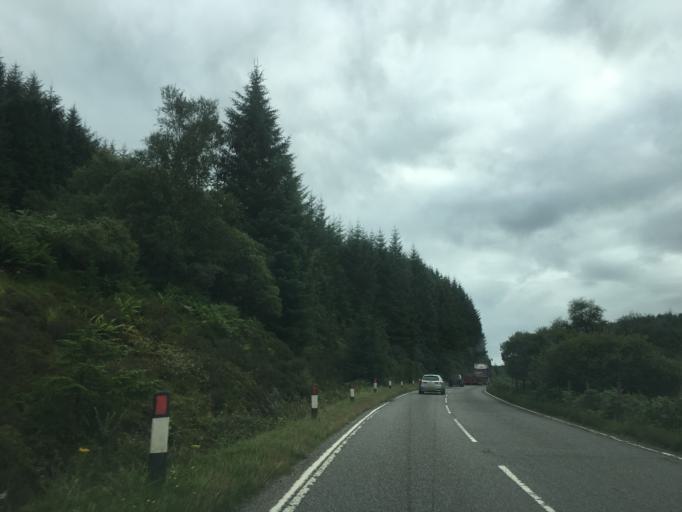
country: GB
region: Scotland
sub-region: Argyll and Bute
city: Oban
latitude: 56.2895
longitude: -5.4711
